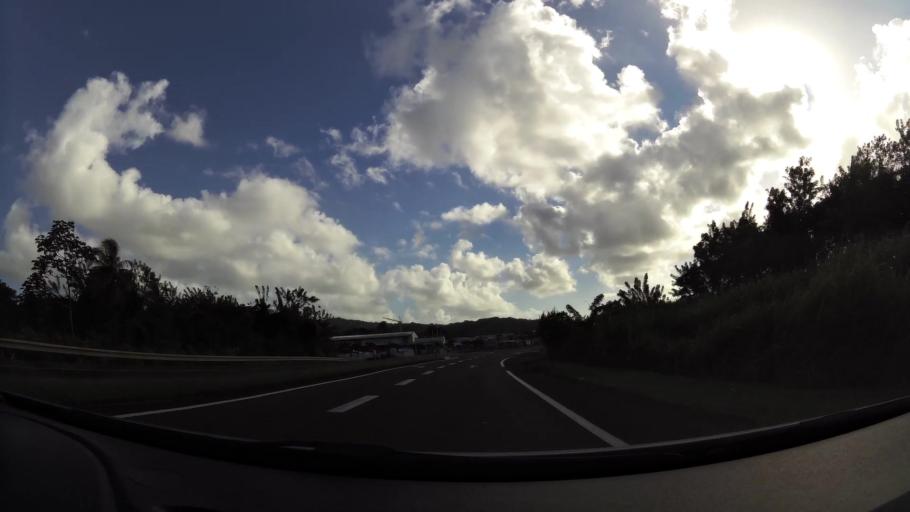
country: MQ
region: Martinique
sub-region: Martinique
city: Ducos
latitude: 14.5999
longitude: -60.9735
